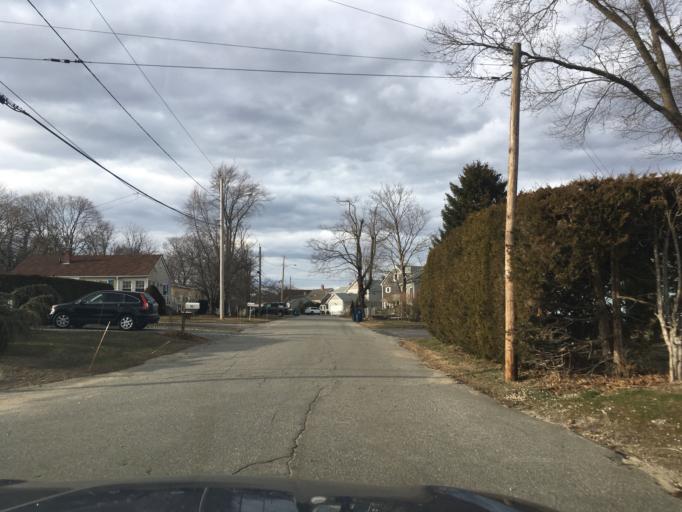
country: US
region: Rhode Island
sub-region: Kent County
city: Warwick
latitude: 41.6659
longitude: -71.4215
